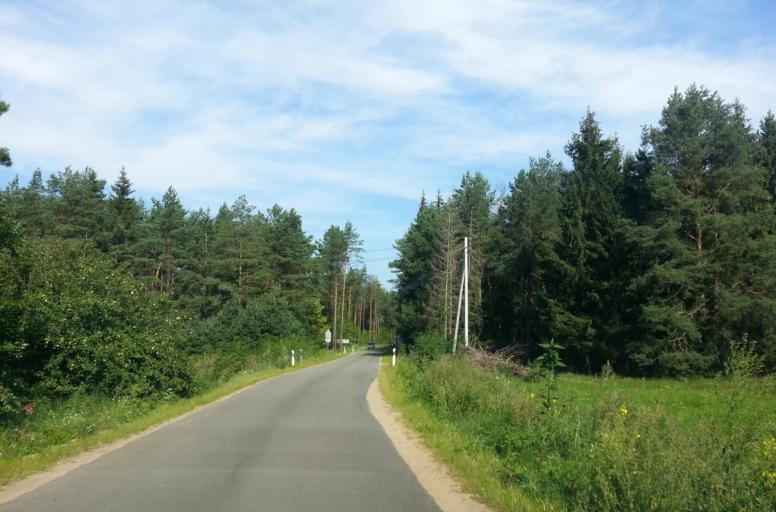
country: LT
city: Grigiskes
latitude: 54.7271
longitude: 25.0464
